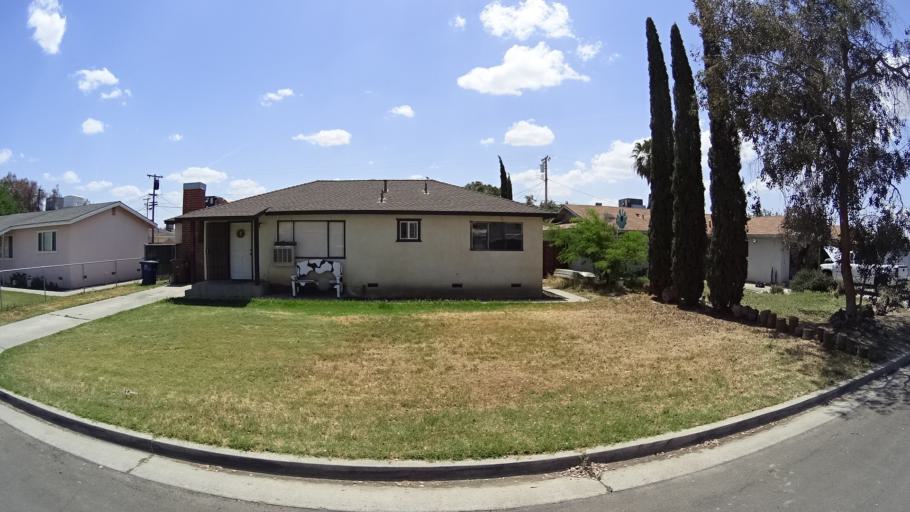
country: US
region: California
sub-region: Kings County
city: Stratford
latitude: 36.1940
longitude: -119.8213
